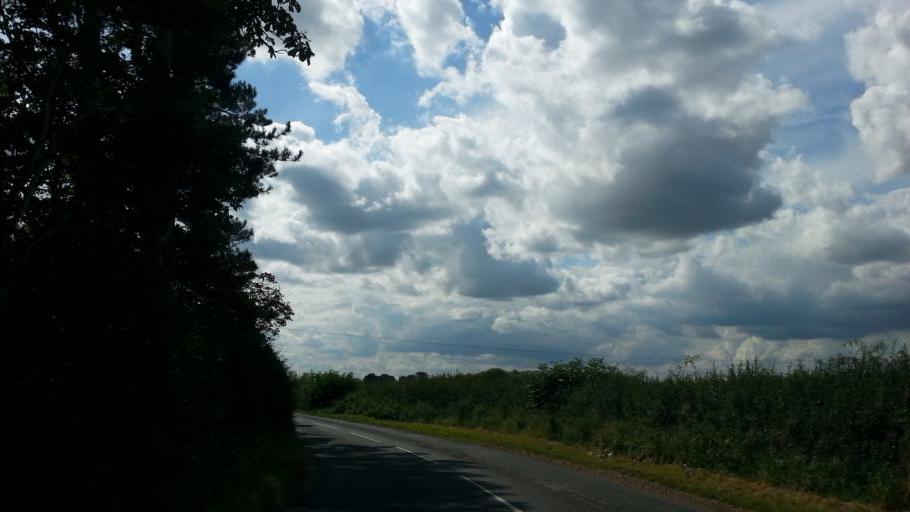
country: GB
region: England
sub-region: Nottinghamshire
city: Newark on Trent
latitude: 53.1036
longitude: -0.8263
